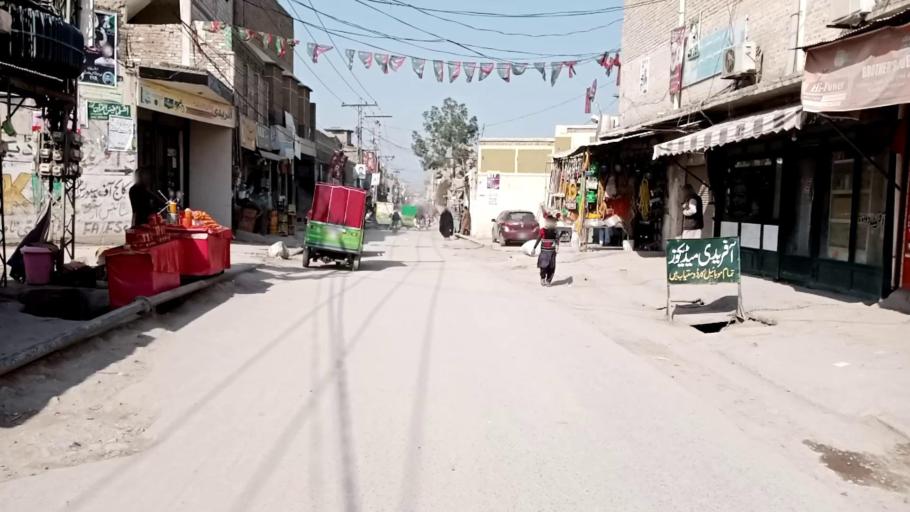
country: PK
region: Khyber Pakhtunkhwa
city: Peshawar
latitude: 34.0099
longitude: 71.5178
